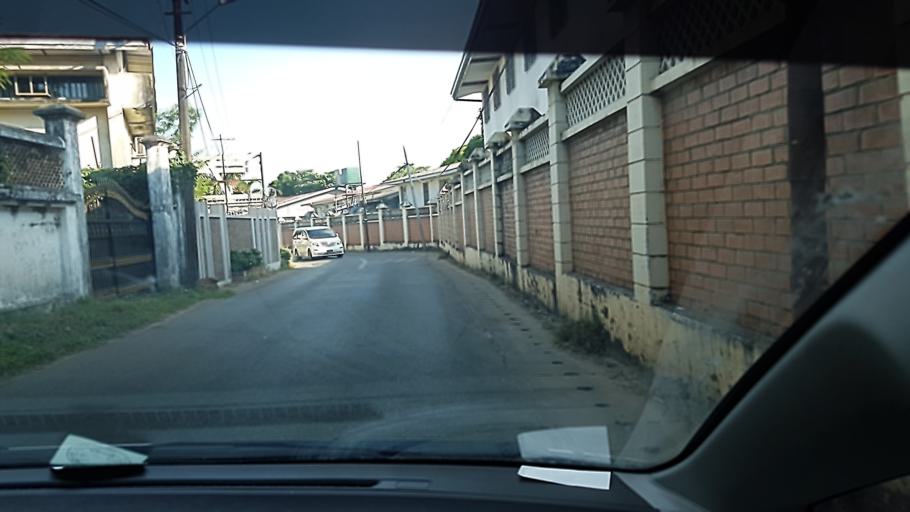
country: MM
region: Yangon
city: Yangon
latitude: 16.8142
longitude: 96.1584
